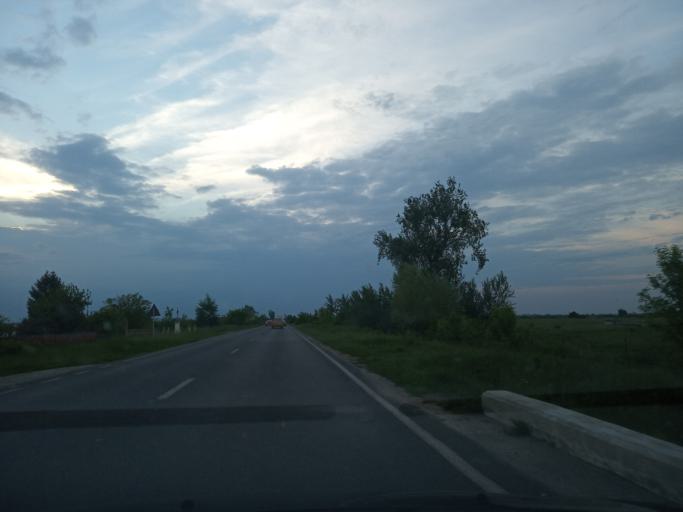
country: RO
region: Timis
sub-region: Comuna Denta
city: Denta
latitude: 45.3658
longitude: 21.2456
